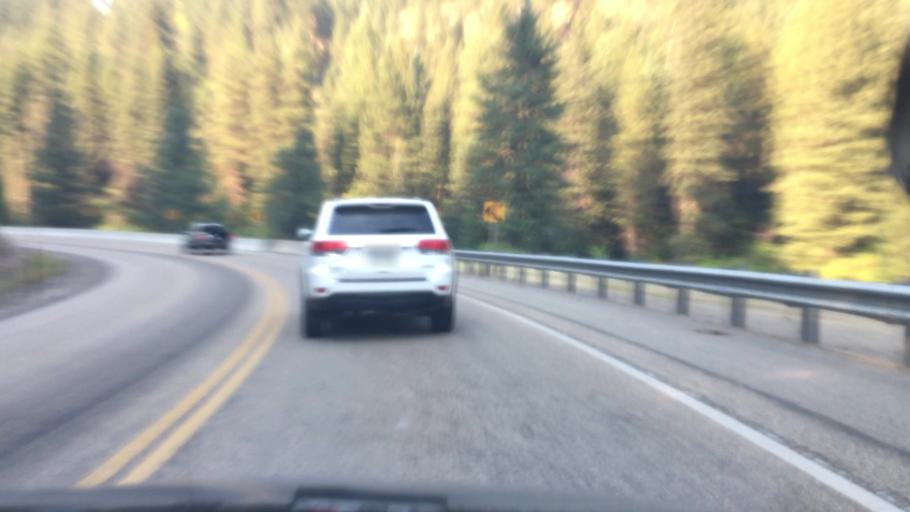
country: US
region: Idaho
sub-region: Valley County
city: Cascade
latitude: 44.1781
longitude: -116.1150
